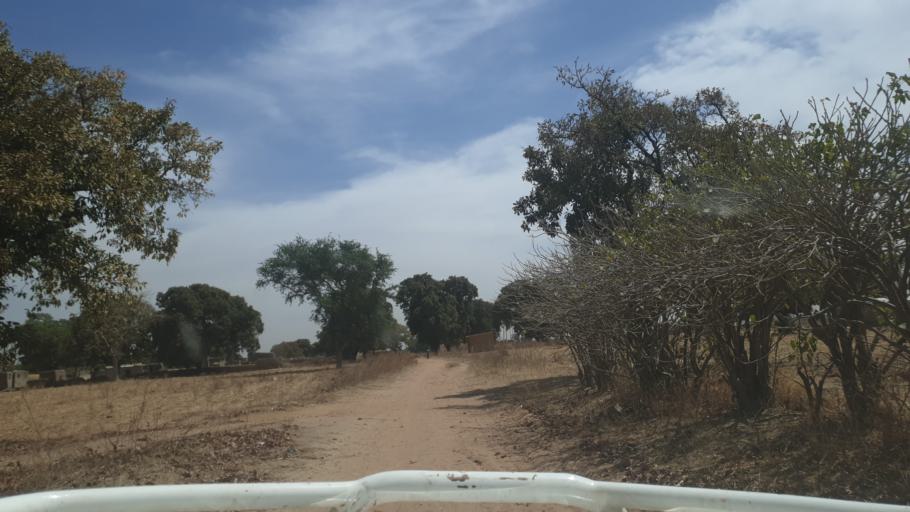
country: ML
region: Sikasso
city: Yorosso
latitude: 12.2913
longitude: -4.6581
